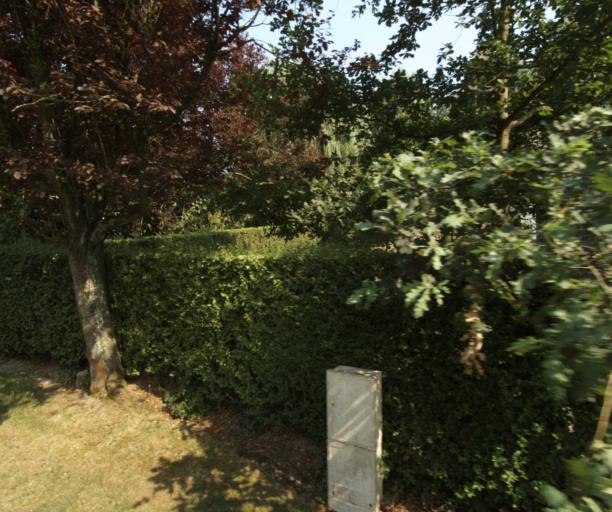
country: FR
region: Nord-Pas-de-Calais
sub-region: Departement du Nord
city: Bondues
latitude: 50.7248
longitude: 3.1047
